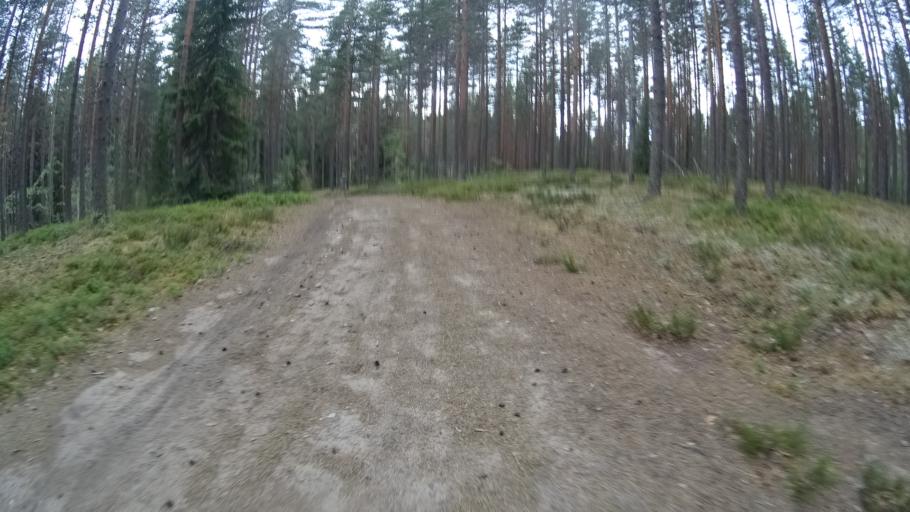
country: FI
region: Satakunta
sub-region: Pohjois-Satakunta
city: Jaemijaervi
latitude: 61.7692
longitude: 22.7569
